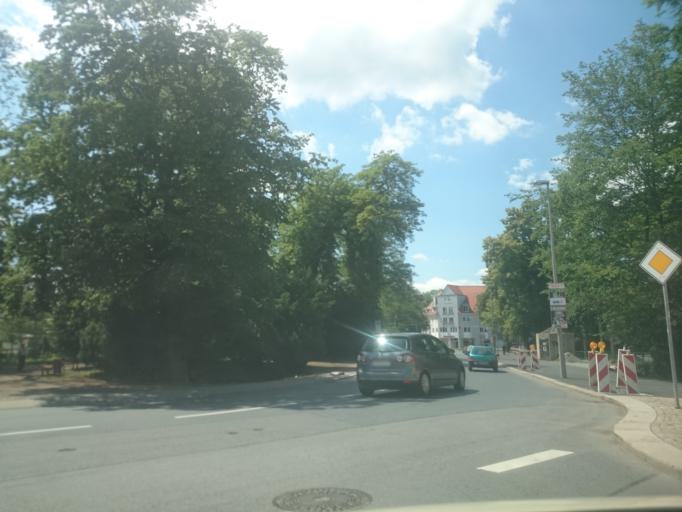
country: DE
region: Saxony
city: Freiberg
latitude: 50.9196
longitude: 13.3399
